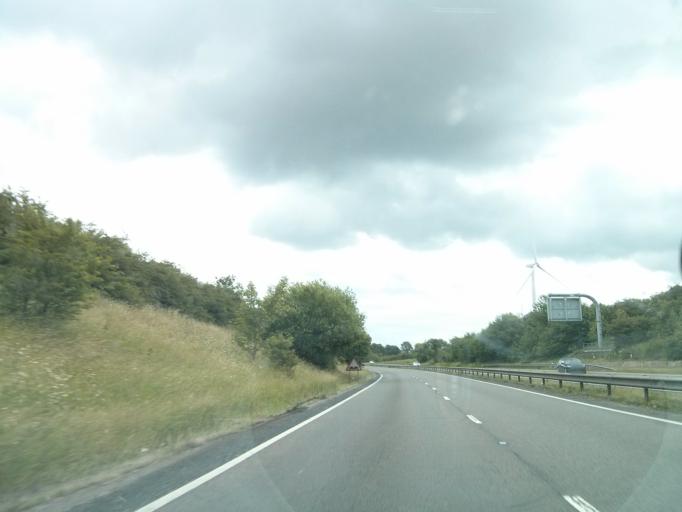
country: GB
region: England
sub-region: Northamptonshire
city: Burton Latimer
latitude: 52.3791
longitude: -0.6615
